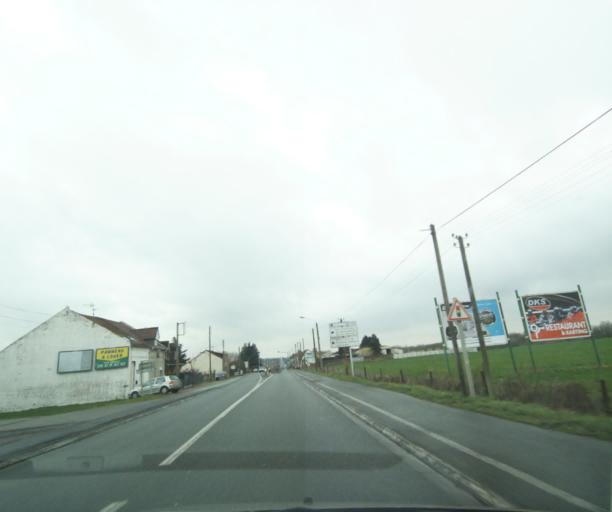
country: FR
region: Nord-Pas-de-Calais
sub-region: Departement du Nord
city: Prouvy
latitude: 50.3289
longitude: 3.4451
